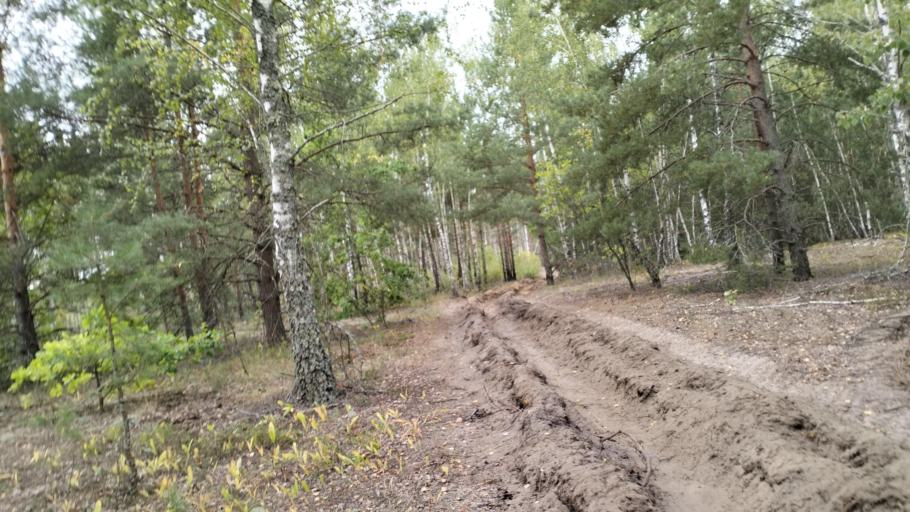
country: BY
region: Brest
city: Davyd-Haradok
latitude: 51.8772
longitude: 27.2129
